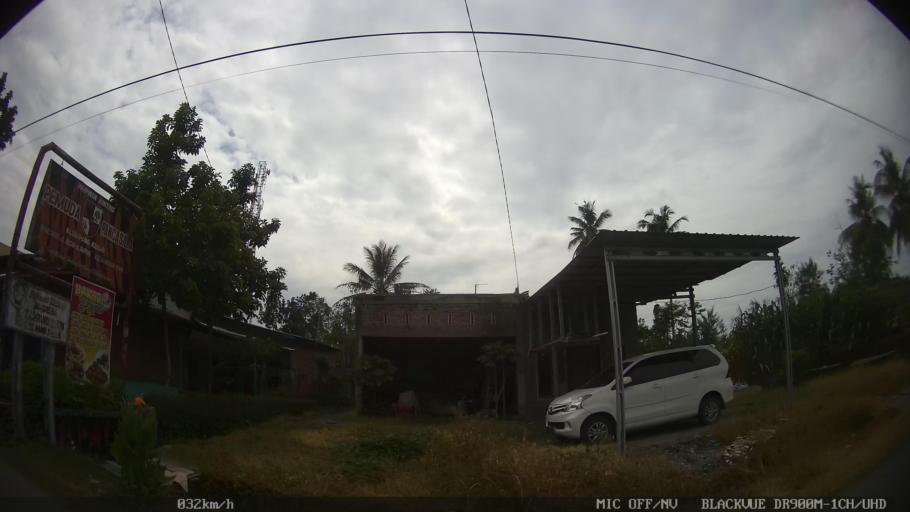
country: ID
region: North Sumatra
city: Sunggal
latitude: 3.6581
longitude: 98.5925
